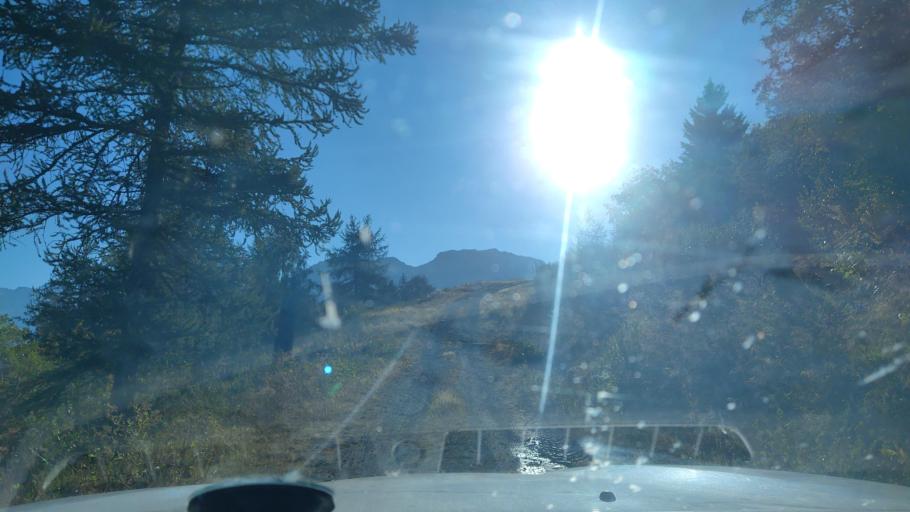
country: FR
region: Rhone-Alpes
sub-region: Departement de la Savoie
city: Valloire
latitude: 45.1739
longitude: 6.4691
